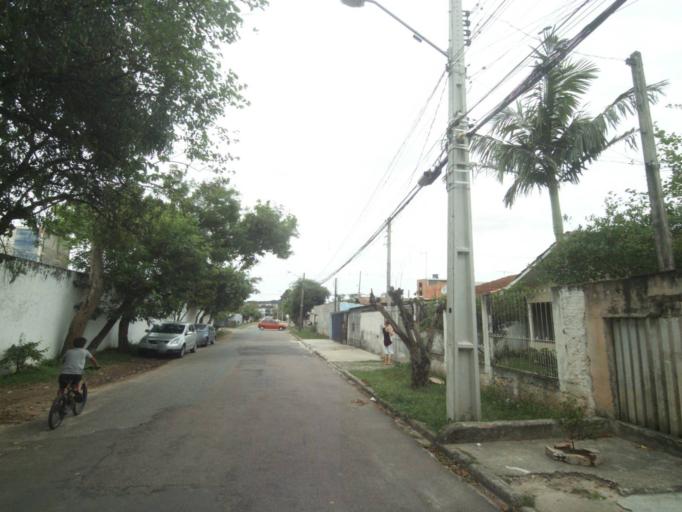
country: BR
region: Parana
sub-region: Curitiba
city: Curitiba
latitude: -25.5140
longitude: -49.3335
